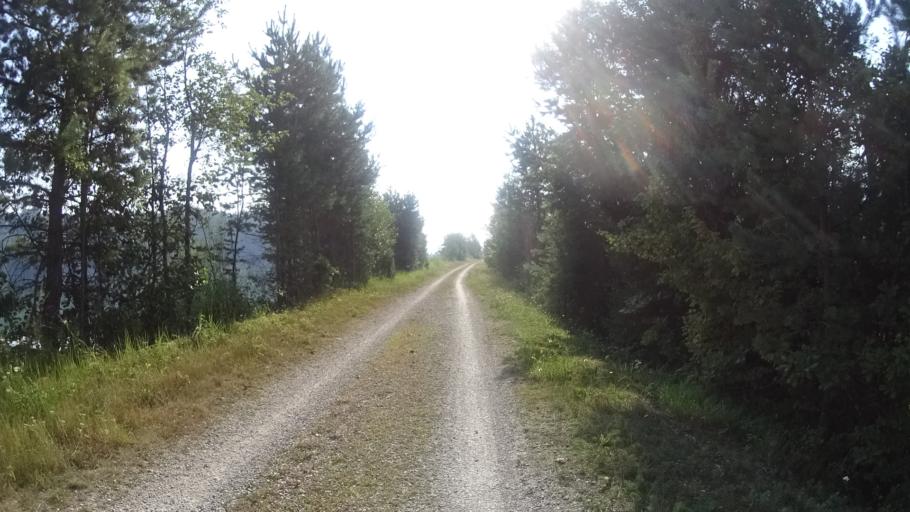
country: AT
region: Carinthia
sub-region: Politischer Bezirk Klagenfurt Land
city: Kottmannsdorf
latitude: 46.5431
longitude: 14.2412
